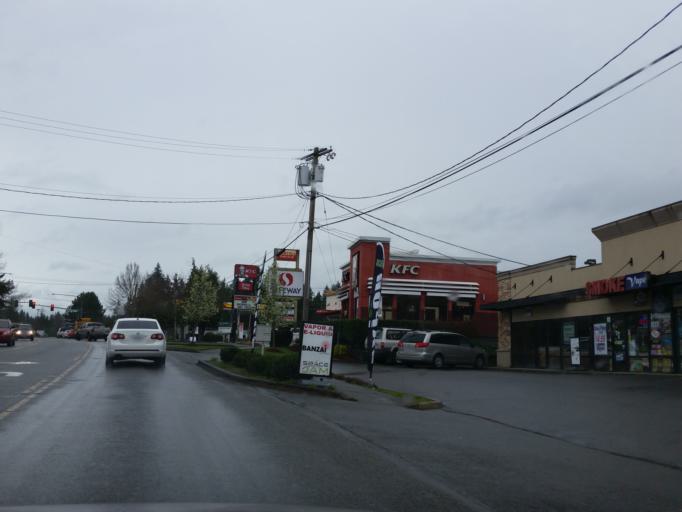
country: US
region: Washington
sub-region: Snohomish County
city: Snohomish
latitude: 47.9257
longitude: -122.0979
